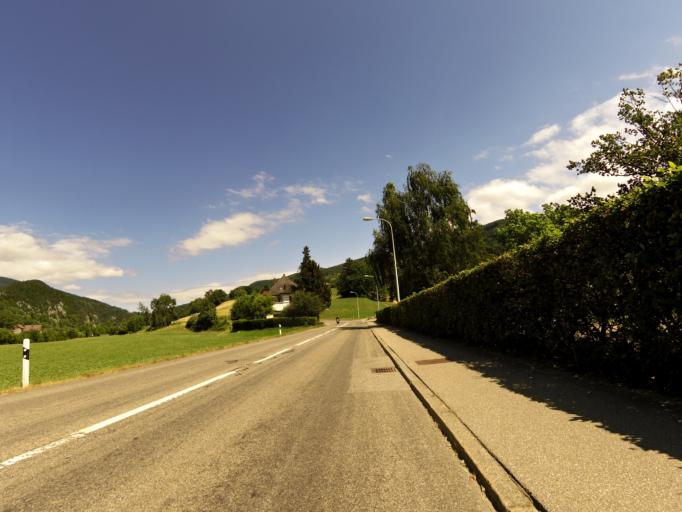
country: CH
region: Solothurn
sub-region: Bezirk Thal
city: Balsthal
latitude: 47.3161
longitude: 7.7006
